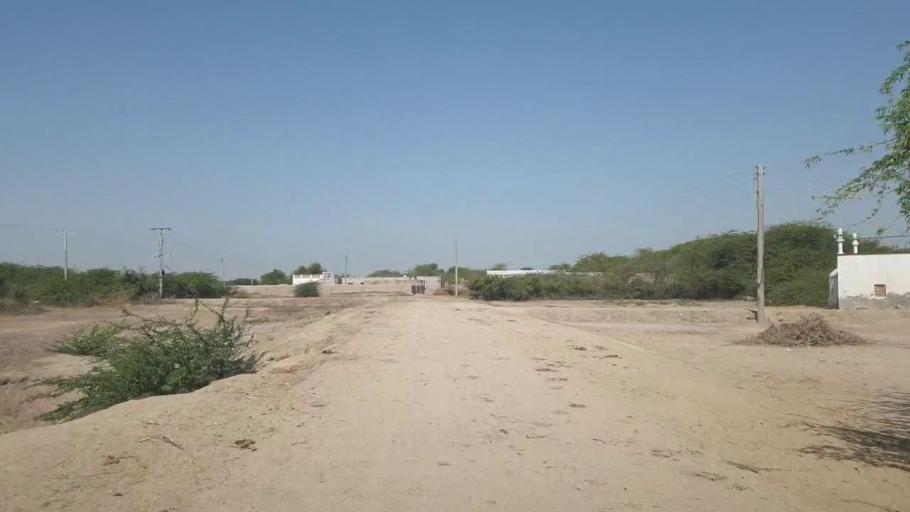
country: PK
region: Sindh
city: Kunri
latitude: 25.2620
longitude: 69.6217
